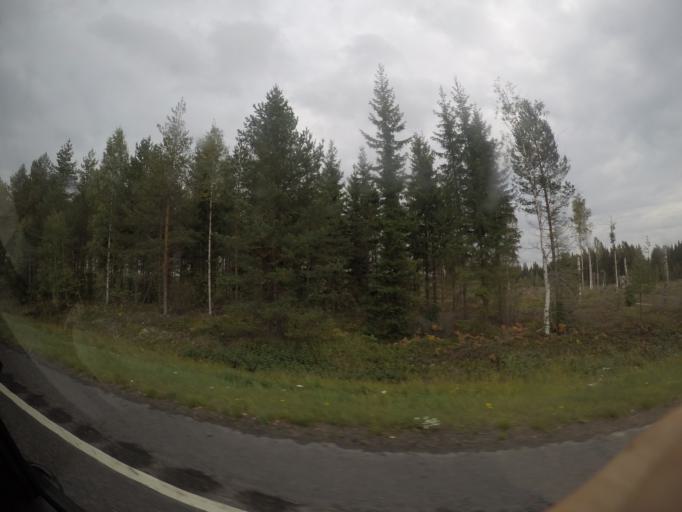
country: FI
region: Haeme
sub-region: Haemeenlinna
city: Parola
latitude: 61.1378
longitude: 24.4160
